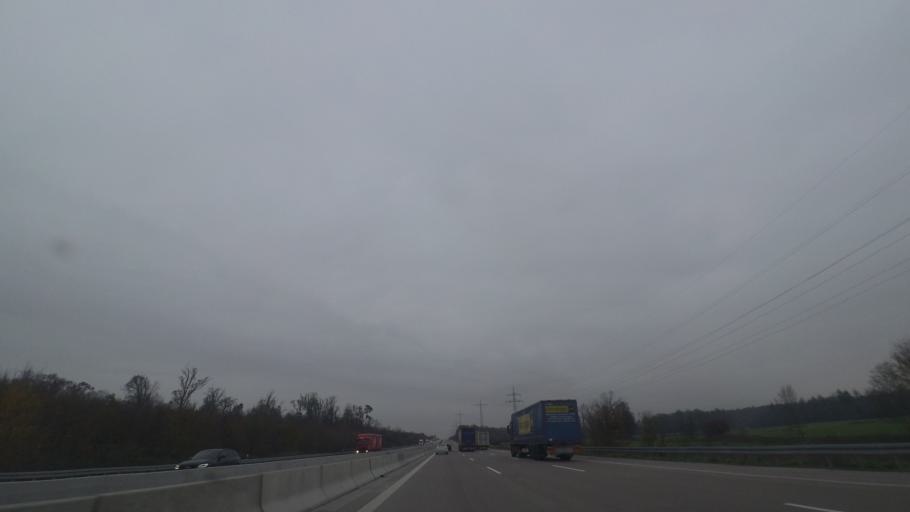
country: DE
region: Baden-Wuerttemberg
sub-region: Karlsruhe Region
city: Malsch
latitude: 48.9105
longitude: 8.3497
